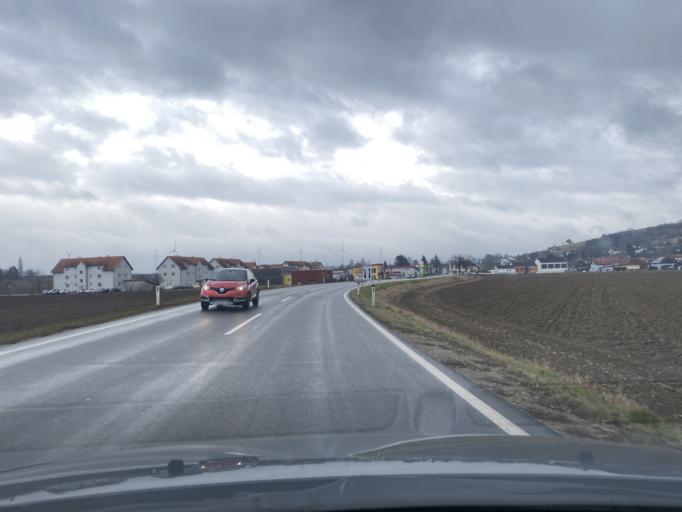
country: AT
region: Lower Austria
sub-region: Politischer Bezirk Sankt Polten
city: Haunoldstein
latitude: 48.1958
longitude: 15.4652
